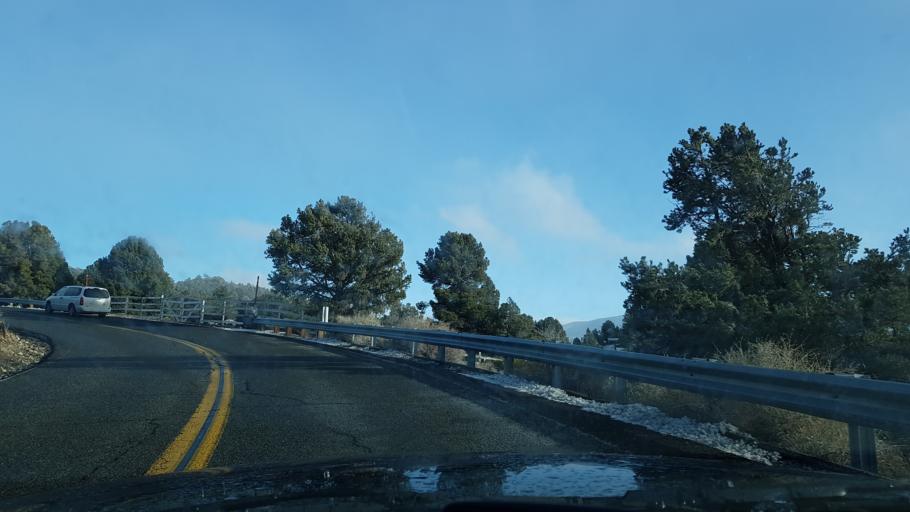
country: US
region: California
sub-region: San Bernardino County
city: Big Bear City
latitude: 34.2894
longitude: -116.8084
